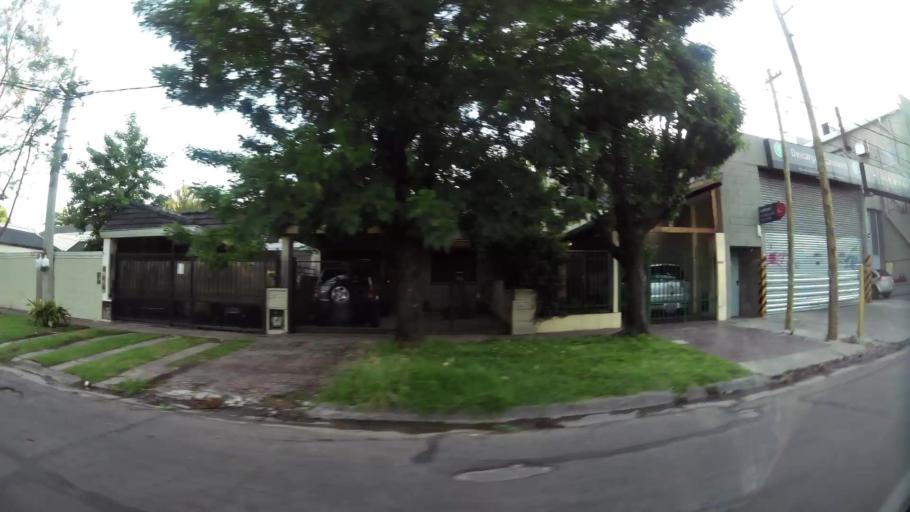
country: AR
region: Buenos Aires
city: Ituzaingo
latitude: -34.6402
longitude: -58.6552
